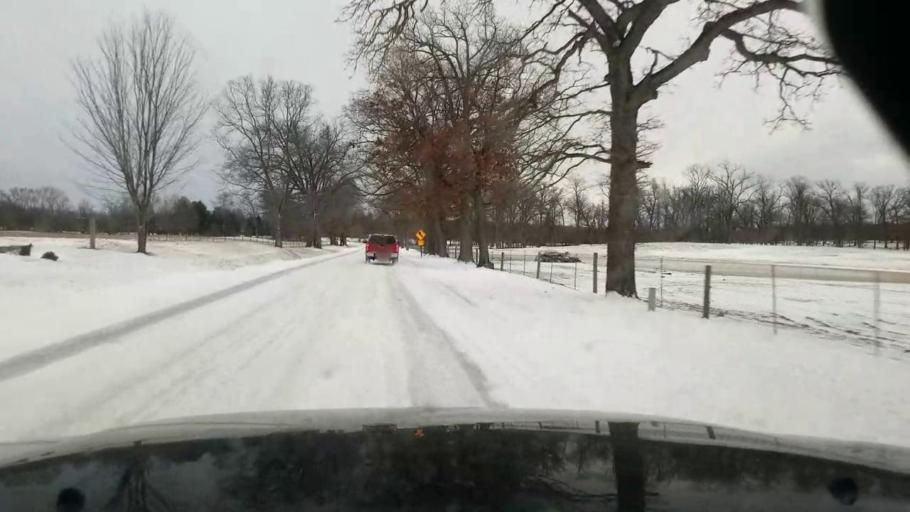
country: US
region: Michigan
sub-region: Jackson County
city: Spring Arbor
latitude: 42.1634
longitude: -84.5002
